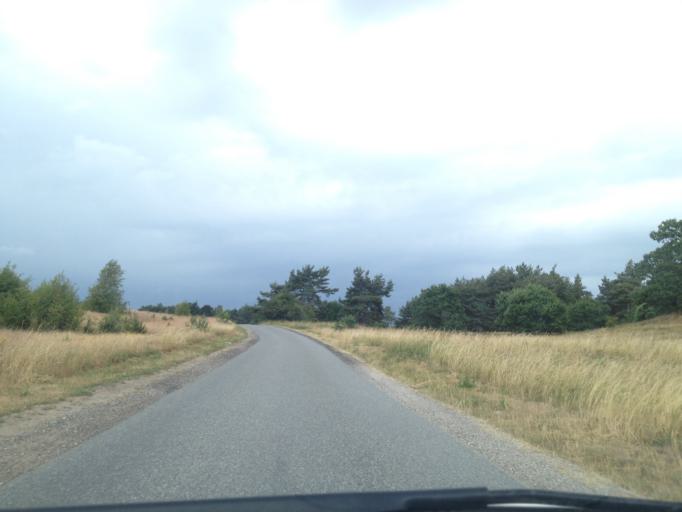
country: DK
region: Central Jutland
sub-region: Syddjurs Kommune
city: Ebeltoft
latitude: 56.1637
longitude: 10.6842
